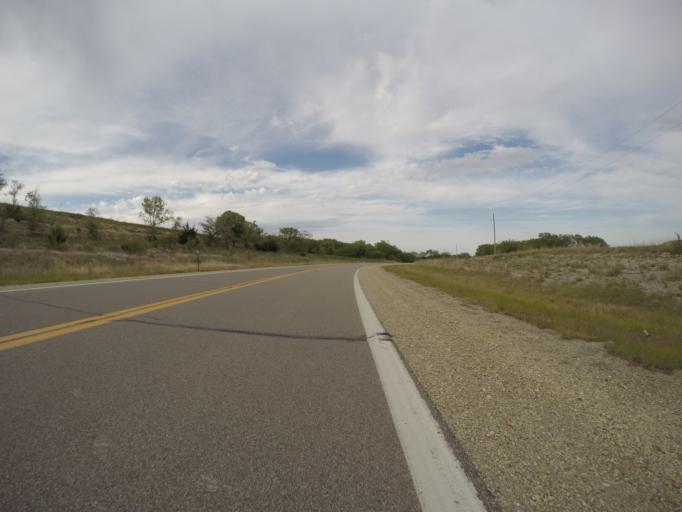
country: US
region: Kansas
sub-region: Riley County
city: Ogden
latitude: 39.1002
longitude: -96.6519
